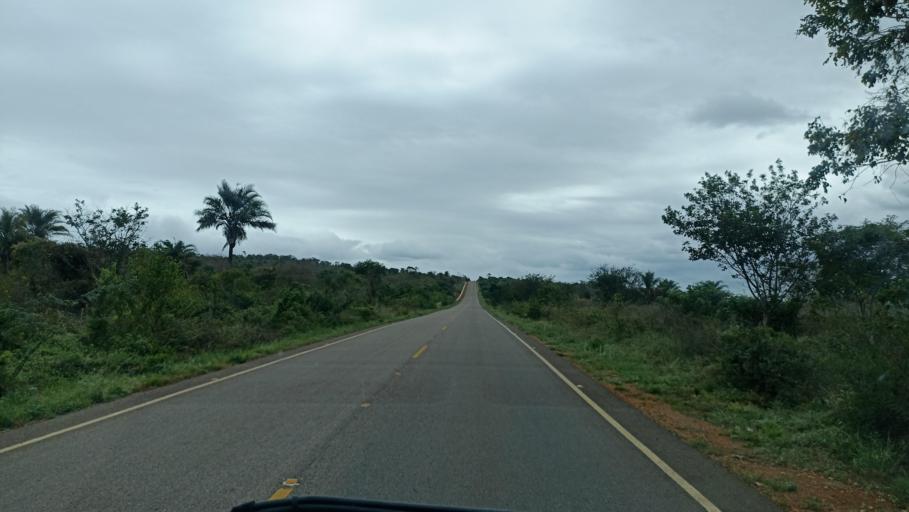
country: BR
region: Bahia
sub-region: Andarai
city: Vera Cruz
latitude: -13.0001
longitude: -40.9915
